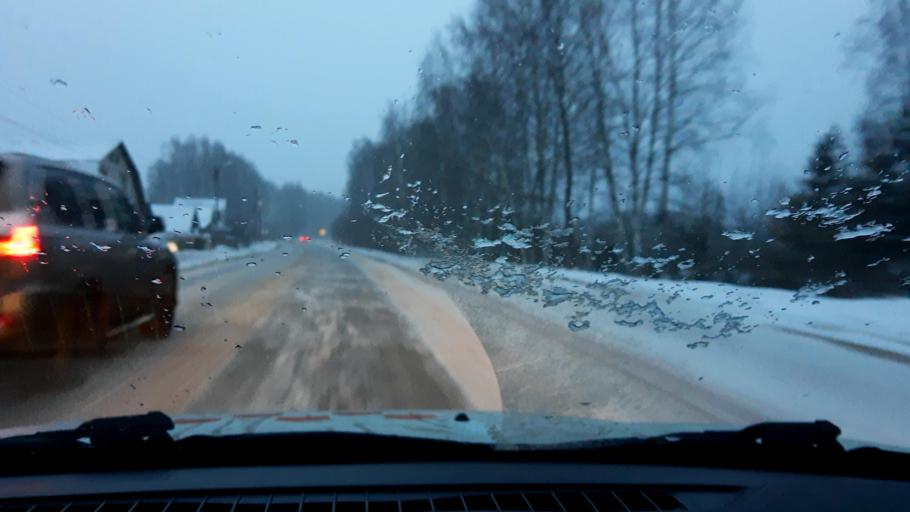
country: RU
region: Nizjnij Novgorod
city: Afonino
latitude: 56.3196
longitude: 44.1578
